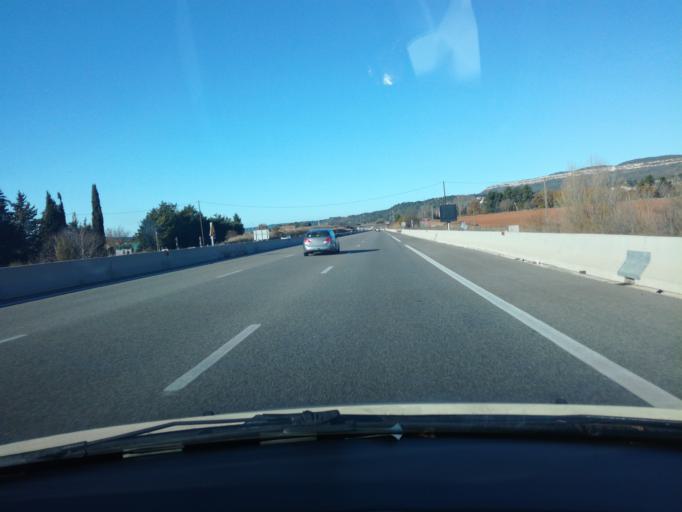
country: FR
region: Provence-Alpes-Cote d'Azur
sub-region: Departement des Bouches-du-Rhone
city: Rousset
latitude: 43.4727
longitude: 5.6352
